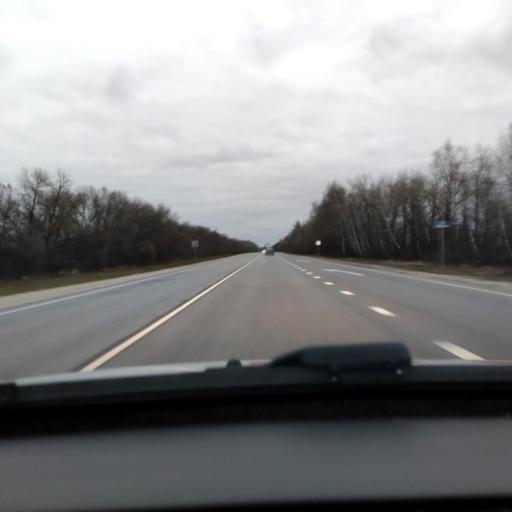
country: RU
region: Lipetsk
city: Borinskoye
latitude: 52.4077
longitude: 39.2439
